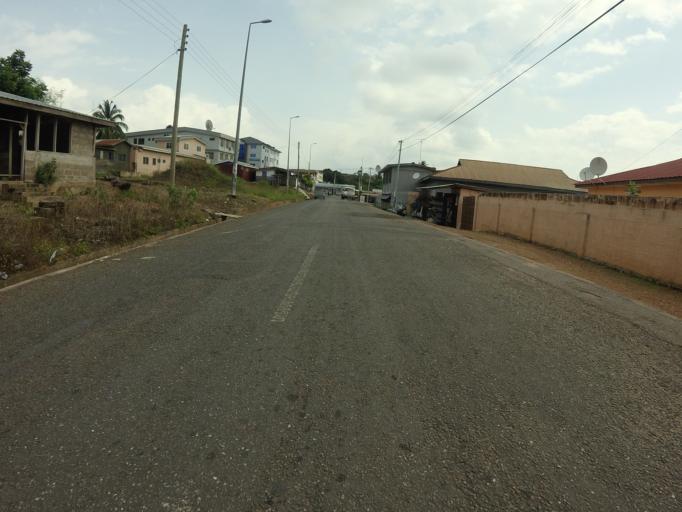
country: GH
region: Volta
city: Ho
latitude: 6.6097
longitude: 0.4723
